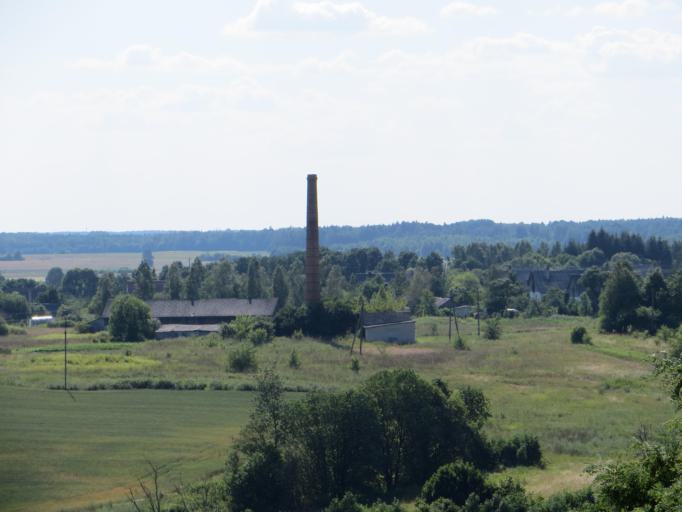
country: LT
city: Sirvintos
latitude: 55.0724
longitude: 25.0702
